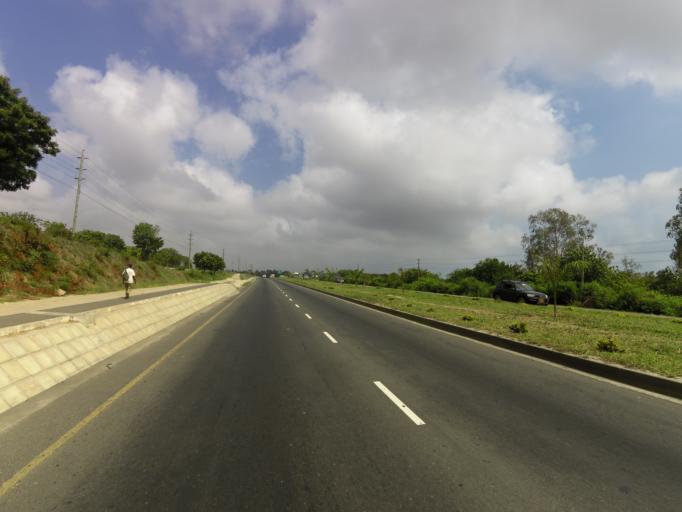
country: TZ
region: Dar es Salaam
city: Magomeni
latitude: -6.7425
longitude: 39.2180
